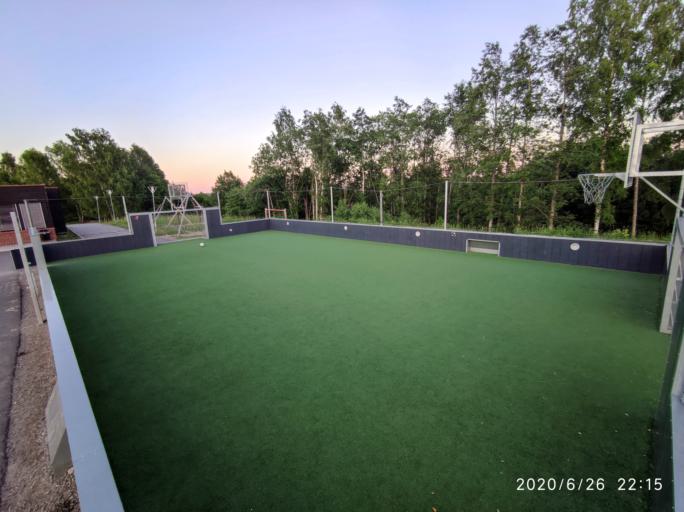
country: NO
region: Akershus
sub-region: Nannestad
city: Teigebyen
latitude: 60.1711
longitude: 10.9949
